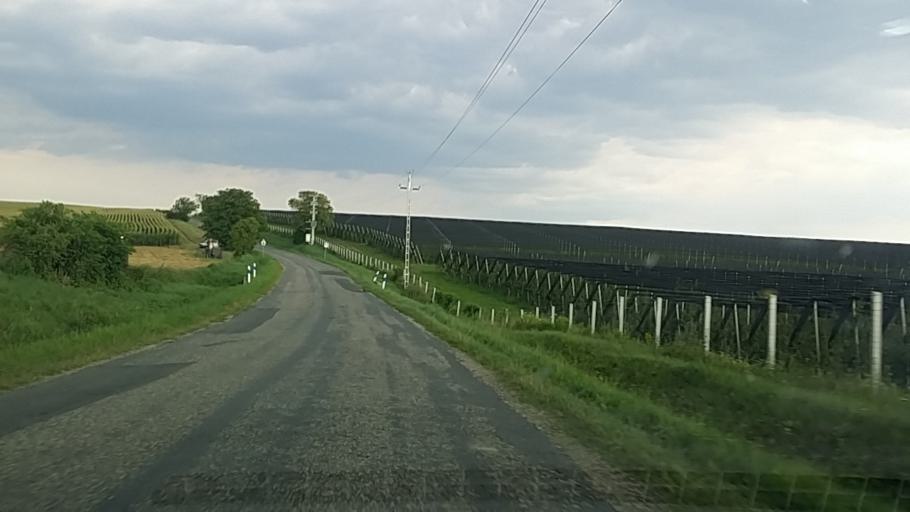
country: HU
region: Zala
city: Nagykanizsa
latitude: 46.4969
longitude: 17.0644
